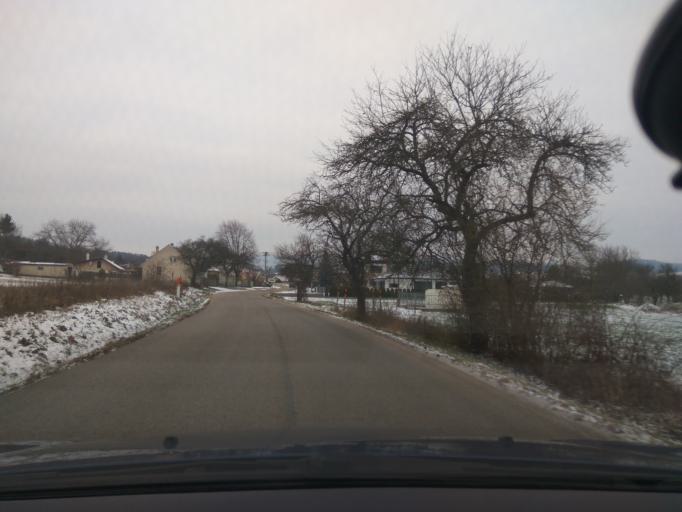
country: SK
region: Nitriansky
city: Stara Tura
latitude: 48.7773
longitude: 17.7413
